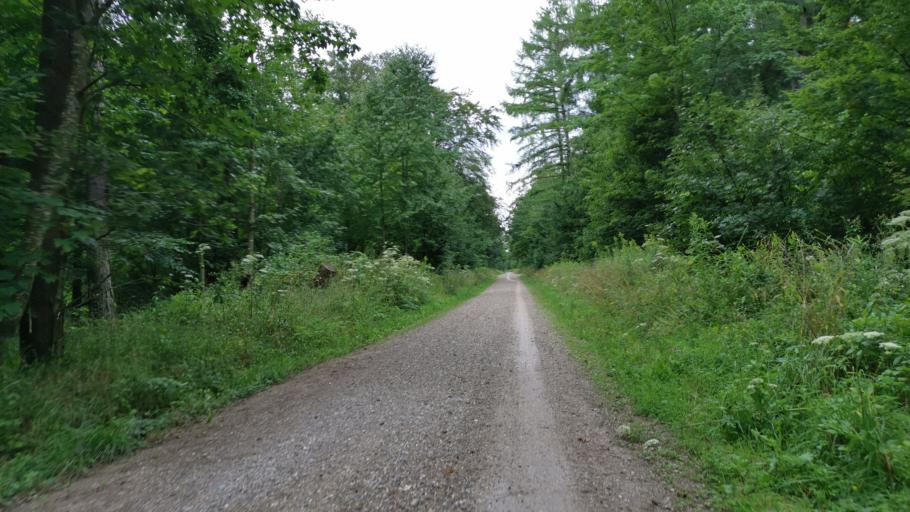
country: DE
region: Bavaria
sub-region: Upper Bavaria
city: Pullach im Isartal
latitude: 48.0747
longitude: 11.5574
